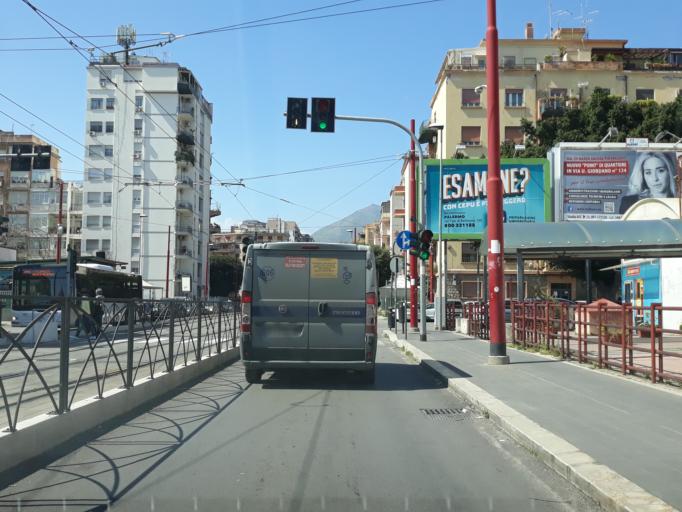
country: IT
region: Sicily
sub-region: Palermo
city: Palermo
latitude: 38.1316
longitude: 13.3409
